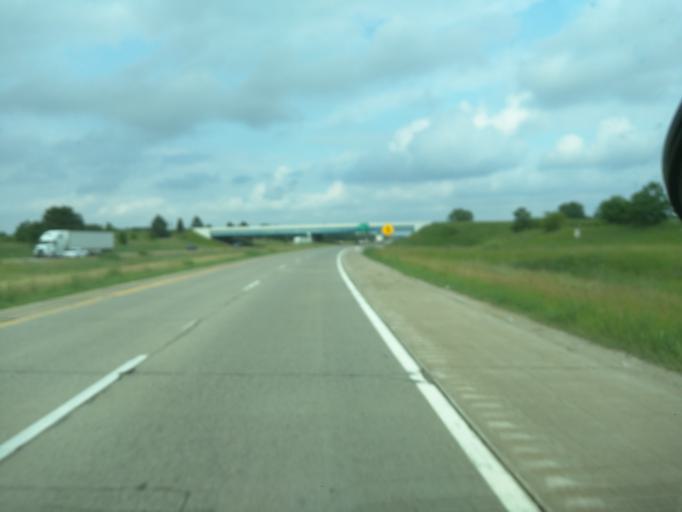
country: US
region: Michigan
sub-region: Clinton County
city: DeWitt
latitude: 42.8158
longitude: -84.5751
